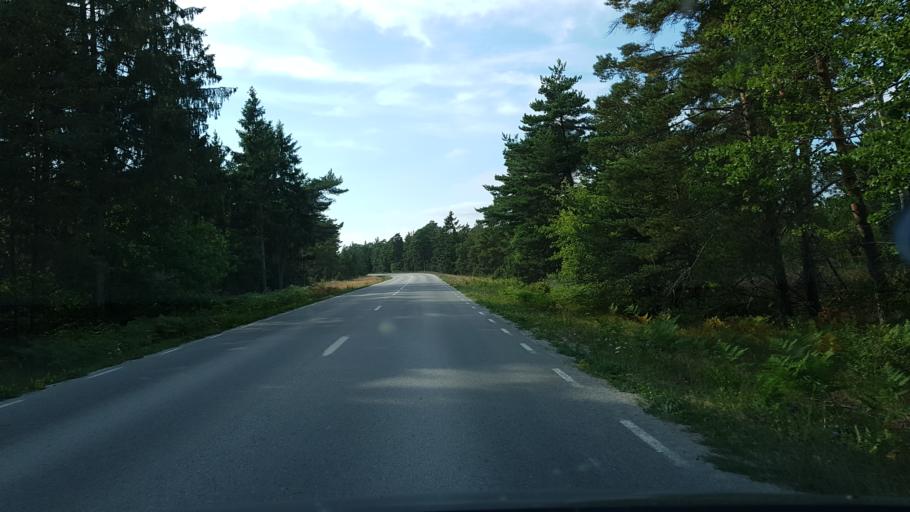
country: SE
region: Gotland
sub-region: Gotland
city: Visby
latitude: 57.6357
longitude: 18.4039
